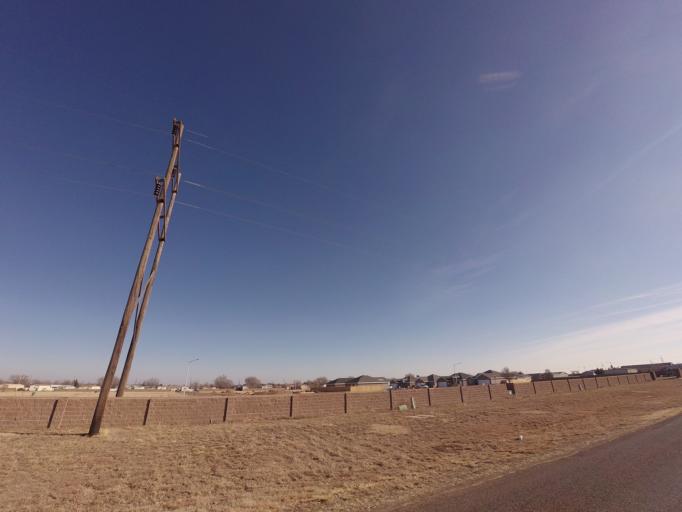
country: US
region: New Mexico
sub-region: Curry County
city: Clovis
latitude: 34.4076
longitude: -103.2493
